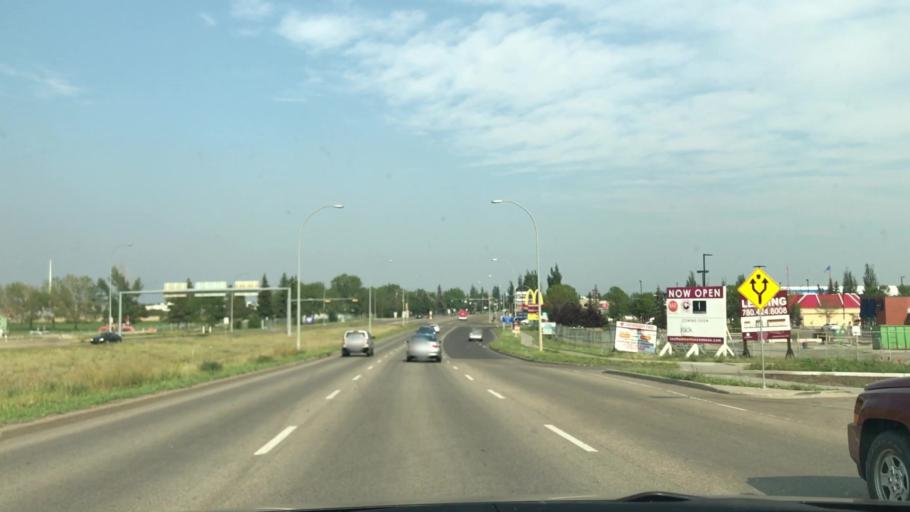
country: CA
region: Alberta
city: Edmonton
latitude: 53.4537
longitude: -113.4895
